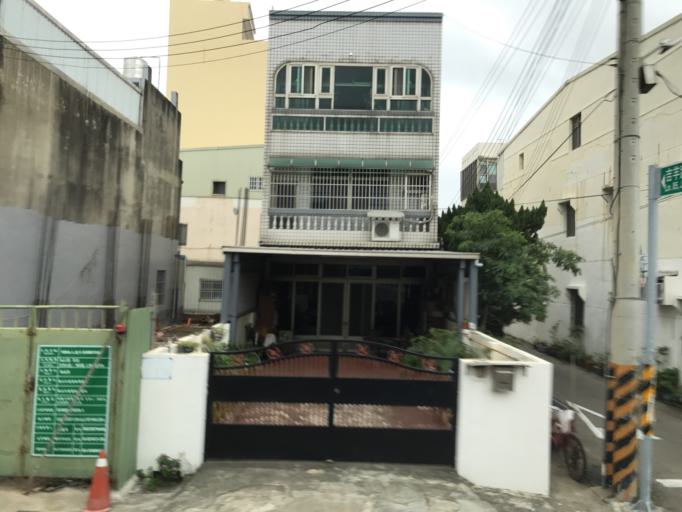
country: TW
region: Taiwan
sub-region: Hsinchu
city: Hsinchu
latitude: 24.8243
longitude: 120.9552
